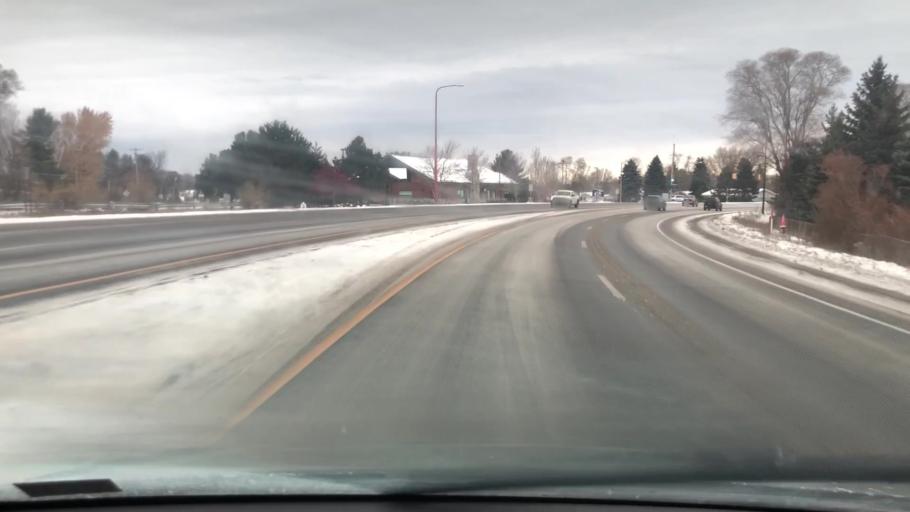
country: US
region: Michigan
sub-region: Grand Traverse County
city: Traverse City
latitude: 44.7301
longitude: -85.6357
